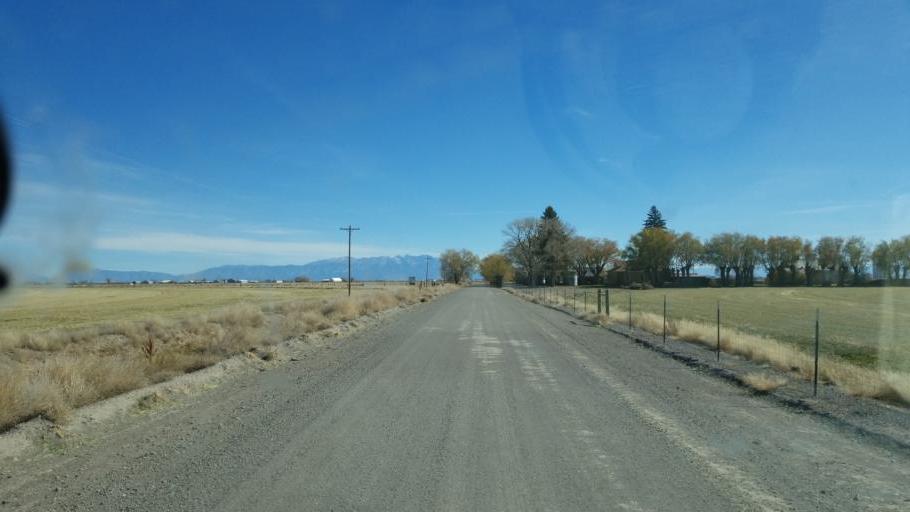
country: US
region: Colorado
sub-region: Rio Grande County
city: Monte Vista
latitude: 37.5311
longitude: -106.0619
